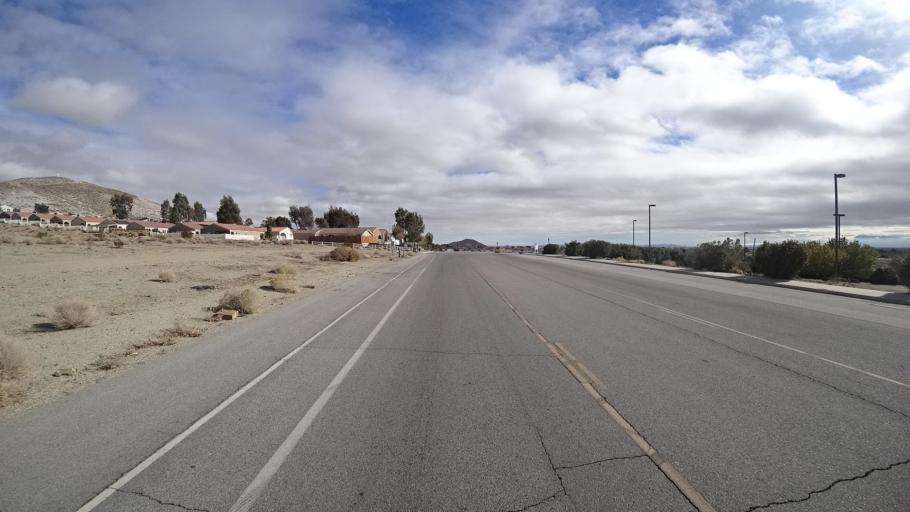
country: US
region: California
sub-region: Kern County
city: Rosamond
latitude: 34.8715
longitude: -118.1767
